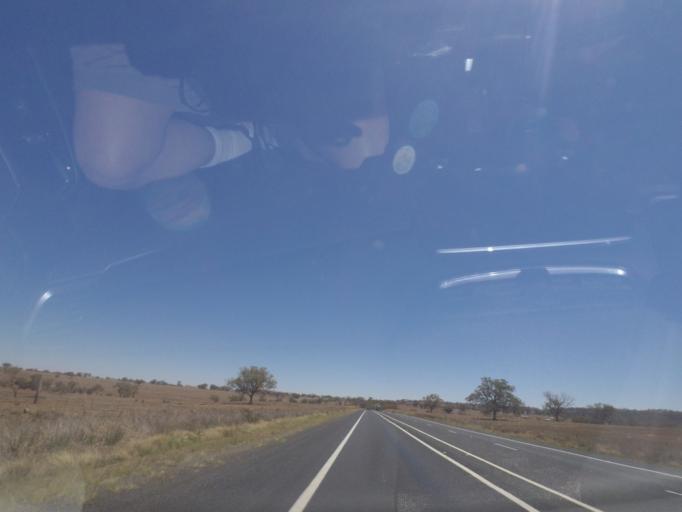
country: AU
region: New South Wales
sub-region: Warrumbungle Shire
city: Coonabarabran
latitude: -31.4189
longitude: 149.1836
